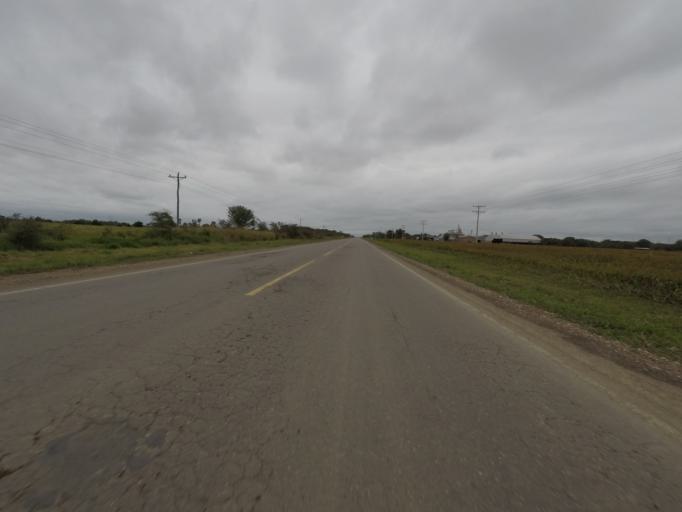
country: BO
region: Santa Cruz
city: Okinawa Numero Uno
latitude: -17.2433
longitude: -62.5554
